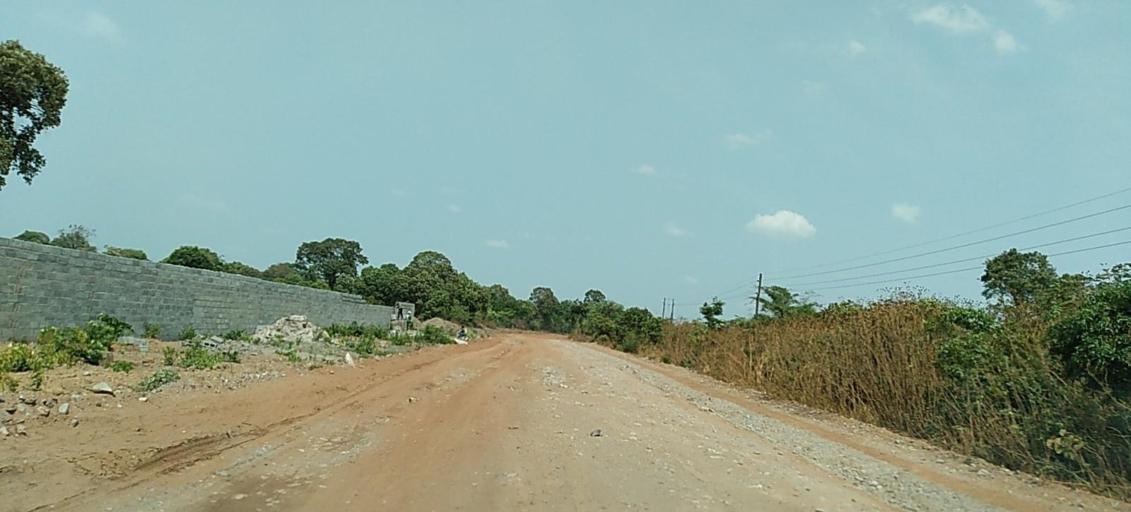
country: ZM
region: Copperbelt
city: Luanshya
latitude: -13.0933
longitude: 28.3105
